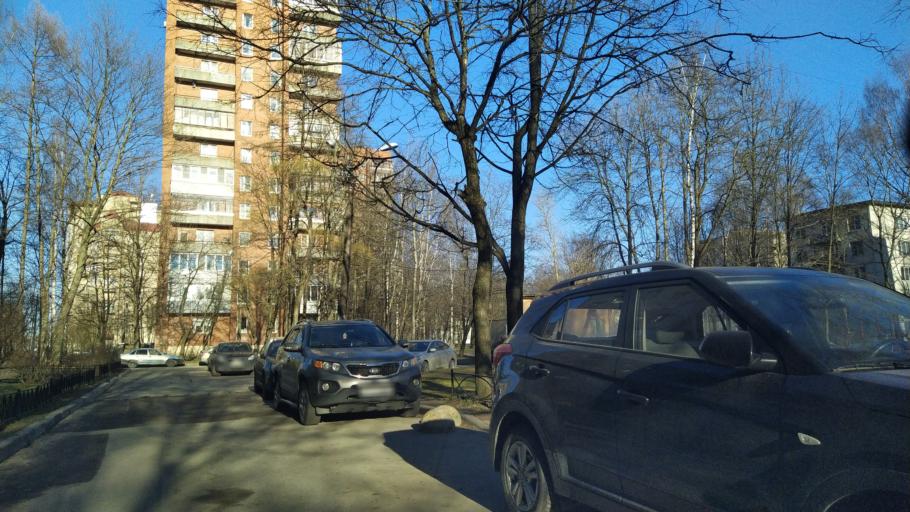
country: RU
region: St.-Petersburg
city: Grazhdanka
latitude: 60.0408
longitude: 30.4008
